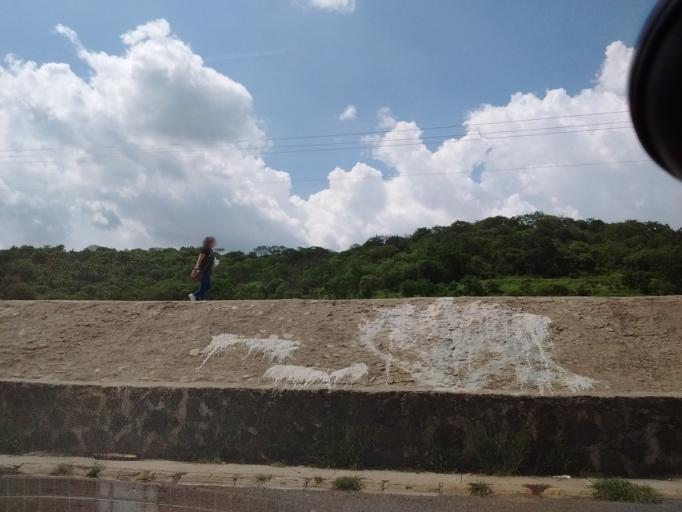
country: MX
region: Jalisco
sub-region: Atotonilco el Alto
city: Vistas del Maguey [Fraccionamiento]
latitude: 20.5282
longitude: -102.5255
